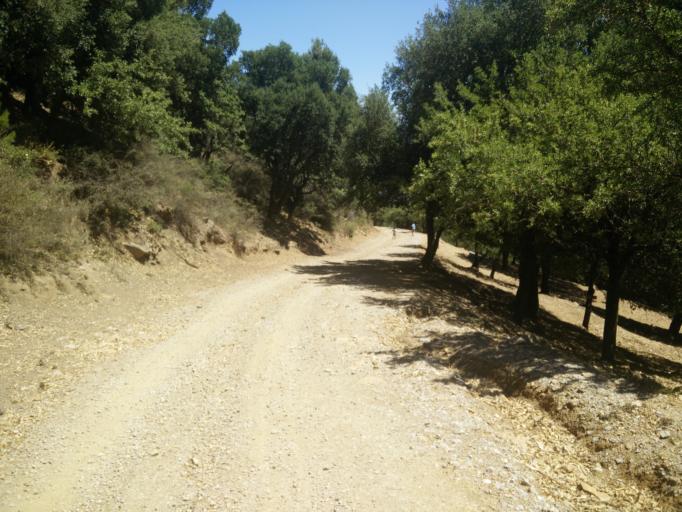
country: IT
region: Sicily
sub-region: Palermo
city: Castelbuono
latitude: 37.9031
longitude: 14.0882
